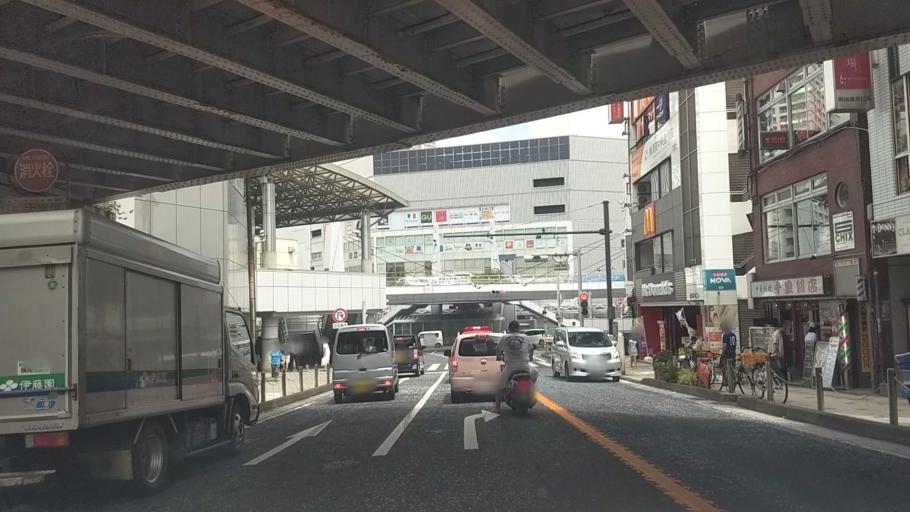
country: JP
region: Kanagawa
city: Yokosuka
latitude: 35.2780
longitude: 139.6709
